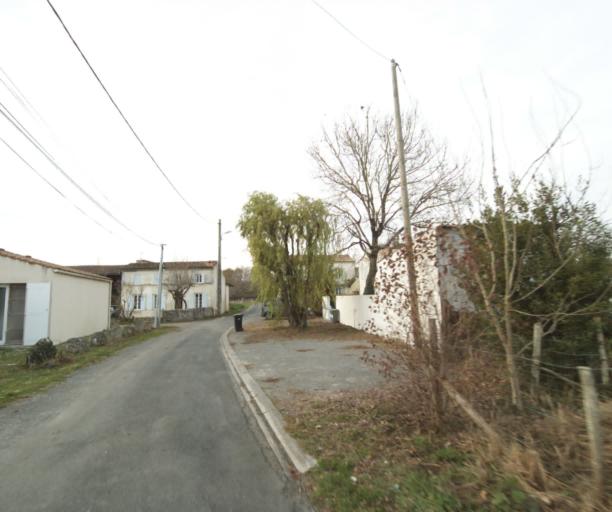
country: FR
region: Poitou-Charentes
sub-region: Departement de la Charente-Maritime
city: Fontcouverte
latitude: 45.7909
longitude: -0.5969
